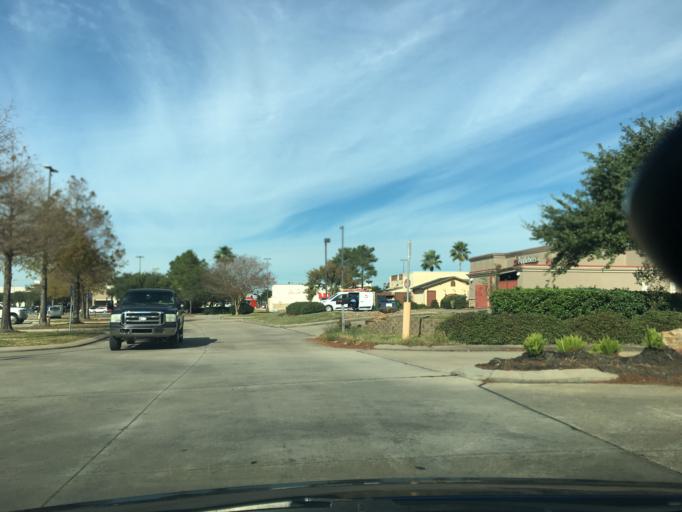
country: US
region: Texas
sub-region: Harris County
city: Cloverleaf
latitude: 29.8101
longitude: -95.1650
